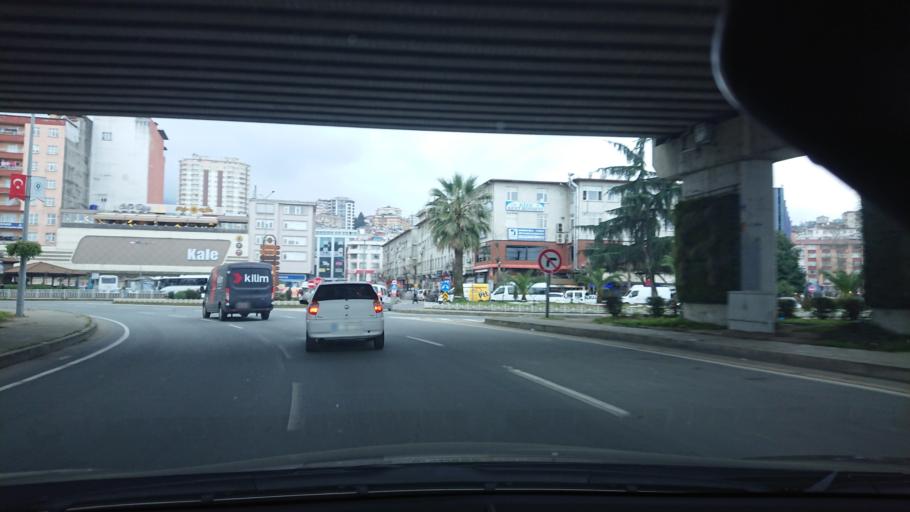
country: TR
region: Rize
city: Rize
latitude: 41.0272
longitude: 40.5187
